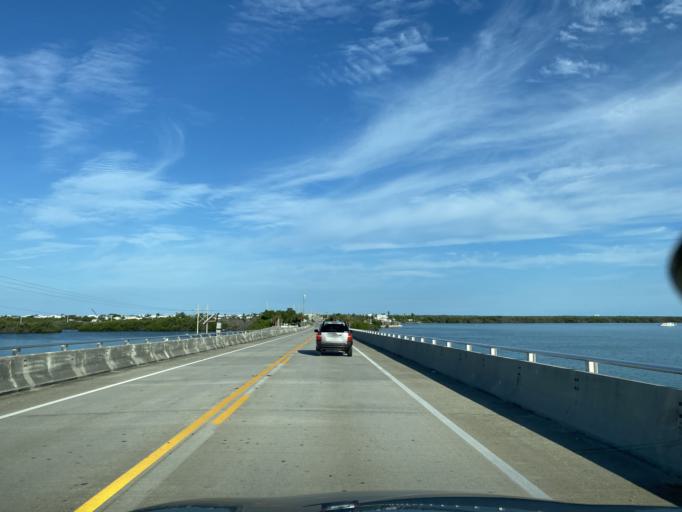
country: US
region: Florida
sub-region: Monroe County
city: Cudjoe Key
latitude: 24.6609
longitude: -81.4340
